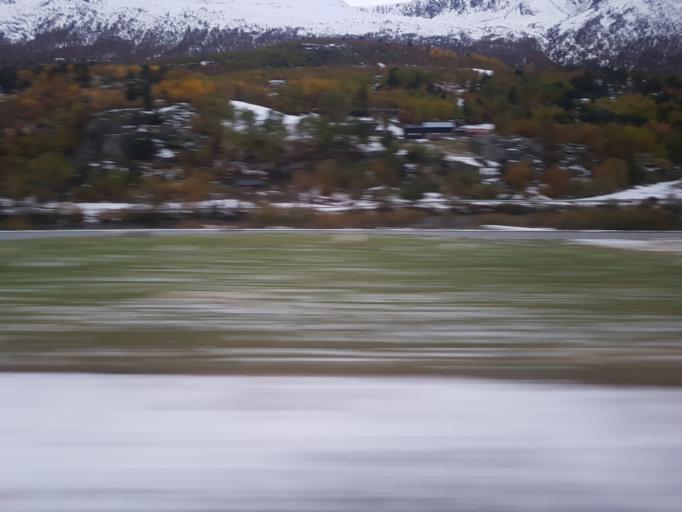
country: NO
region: Sor-Trondelag
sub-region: Oppdal
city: Oppdal
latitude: 62.5191
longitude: 9.6070
